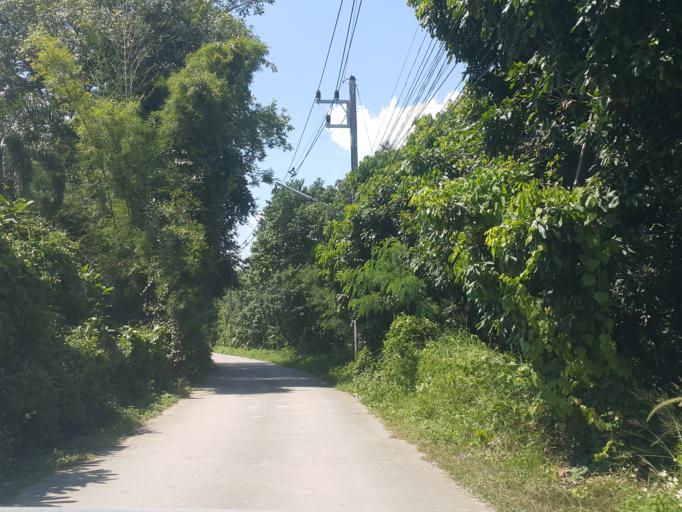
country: TH
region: Chiang Mai
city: Saraphi
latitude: 18.7626
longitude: 99.0471
